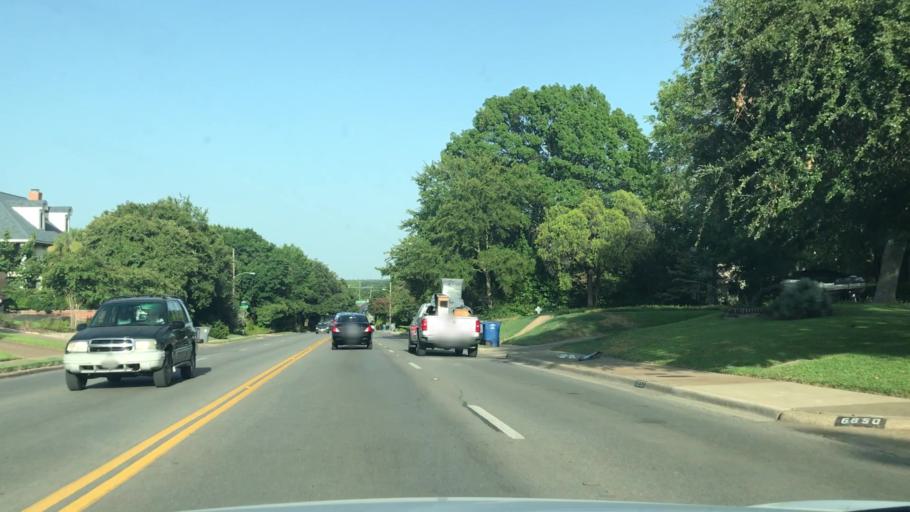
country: US
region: Texas
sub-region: Dallas County
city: Highland Park
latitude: 32.8158
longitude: -96.7410
